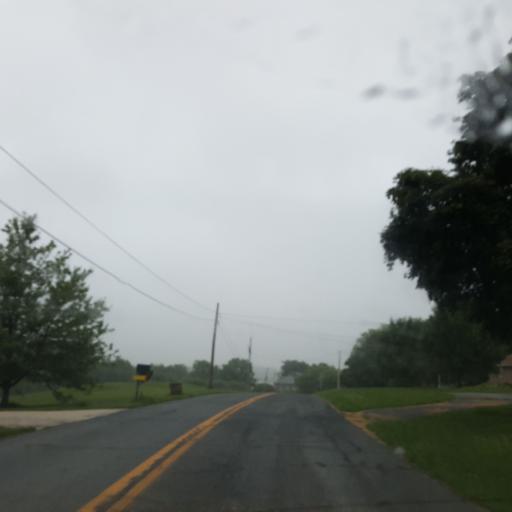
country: US
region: Pennsylvania
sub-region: Lebanon County
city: Palmyra
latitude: 40.4080
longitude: -76.5943
